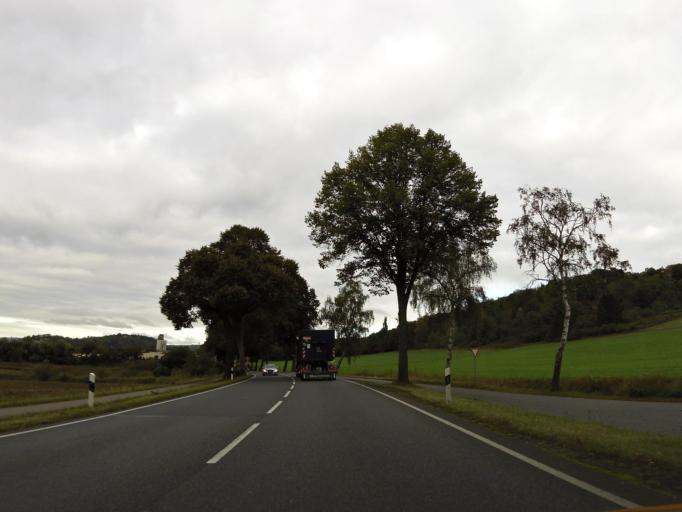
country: DE
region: Lower Saxony
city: Einbeck
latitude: 51.7920
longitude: 9.9316
